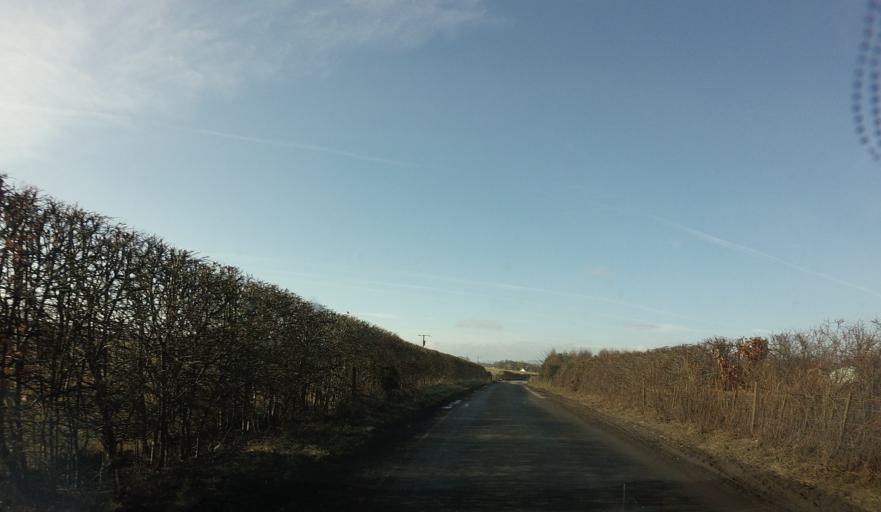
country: GB
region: Scotland
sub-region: Perth and Kinross
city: Stanley
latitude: 56.5252
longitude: -3.4418
